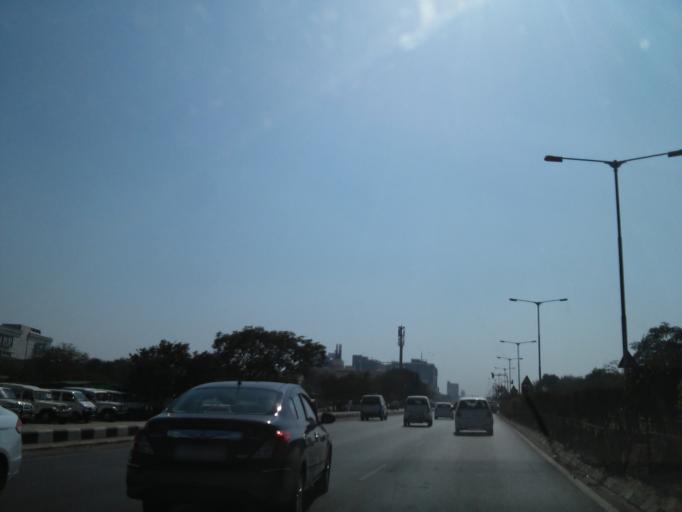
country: IN
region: Gujarat
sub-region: Ahmadabad
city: Ahmedabad
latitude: 23.0820
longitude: 72.5269
